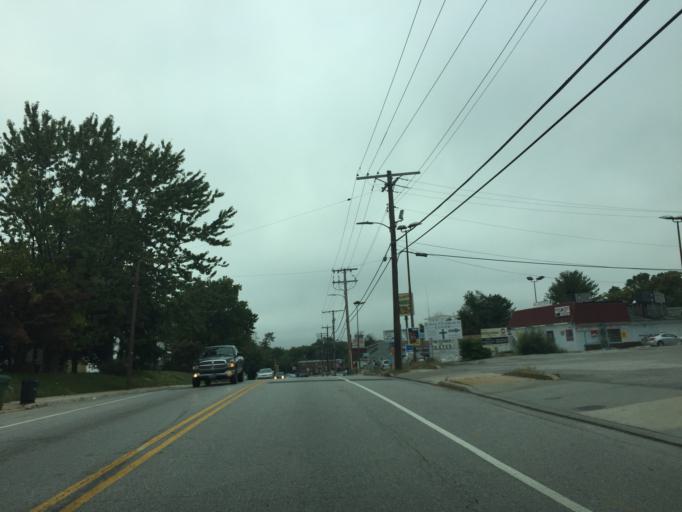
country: US
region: Maryland
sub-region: Baltimore County
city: Rosedale
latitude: 39.3309
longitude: -76.5434
